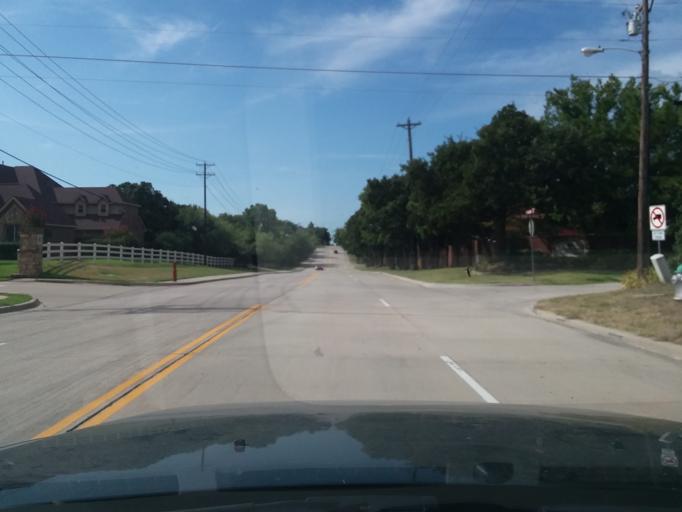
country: US
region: Texas
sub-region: Denton County
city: Flower Mound
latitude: 33.0166
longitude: -97.0885
